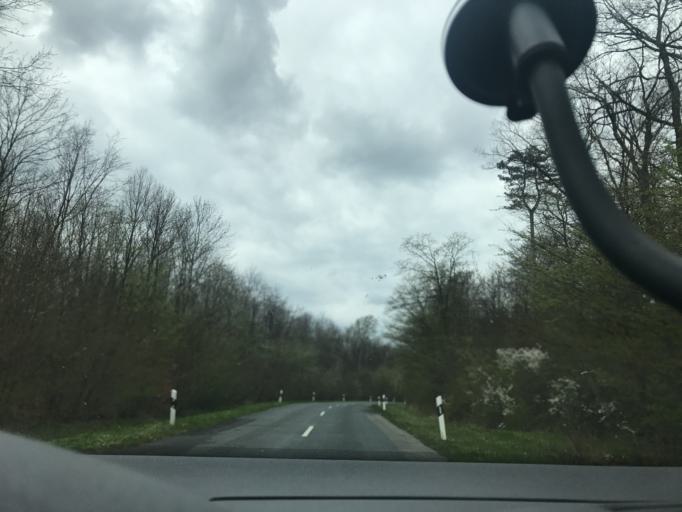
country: DE
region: Lower Saxony
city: Twieflingen
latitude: 52.1518
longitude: 10.9311
